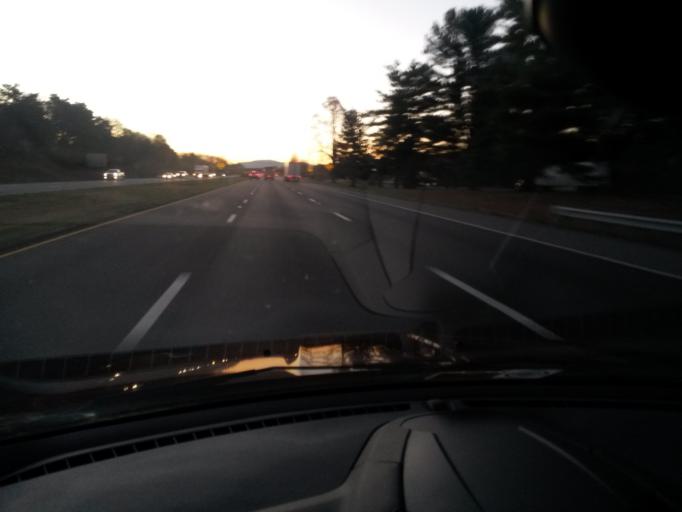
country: US
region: Virginia
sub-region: Roanoke County
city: Hollins
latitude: 37.3128
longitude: -79.9782
